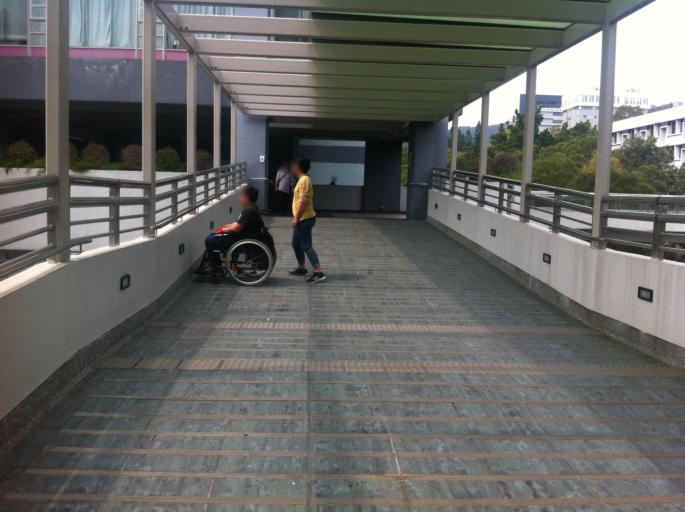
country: HK
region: Sha Tin
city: Sha Tin
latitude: 22.4182
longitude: 114.2074
